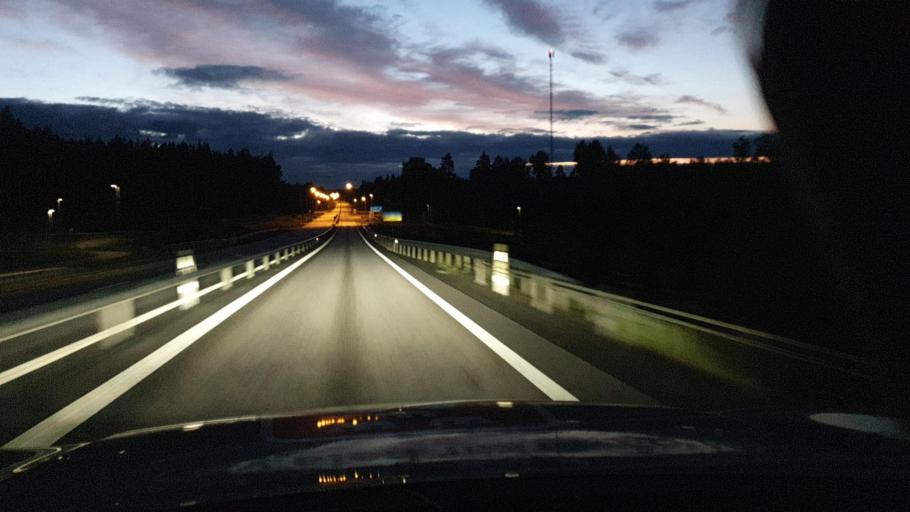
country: SE
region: OErebro
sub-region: Nora Kommun
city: Nora
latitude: 59.4630
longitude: 15.1311
